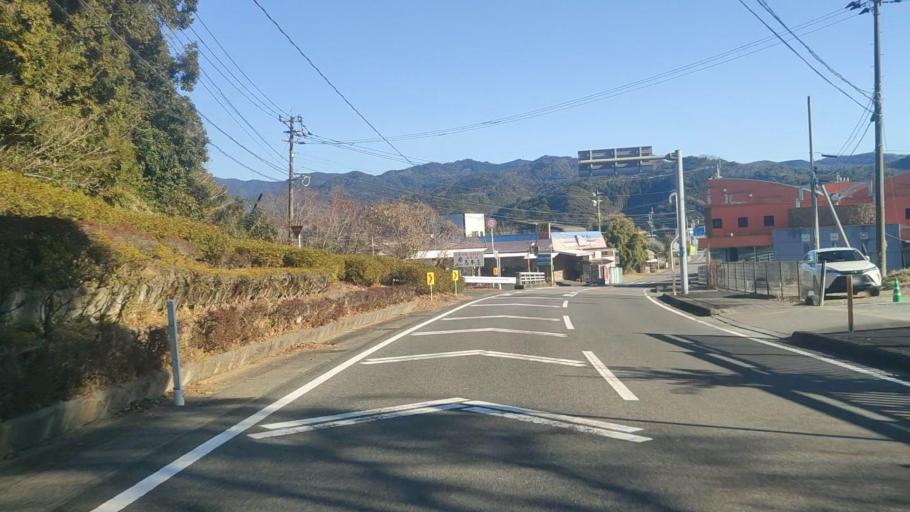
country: JP
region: Miyazaki
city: Nobeoka
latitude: 32.7054
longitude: 131.8164
